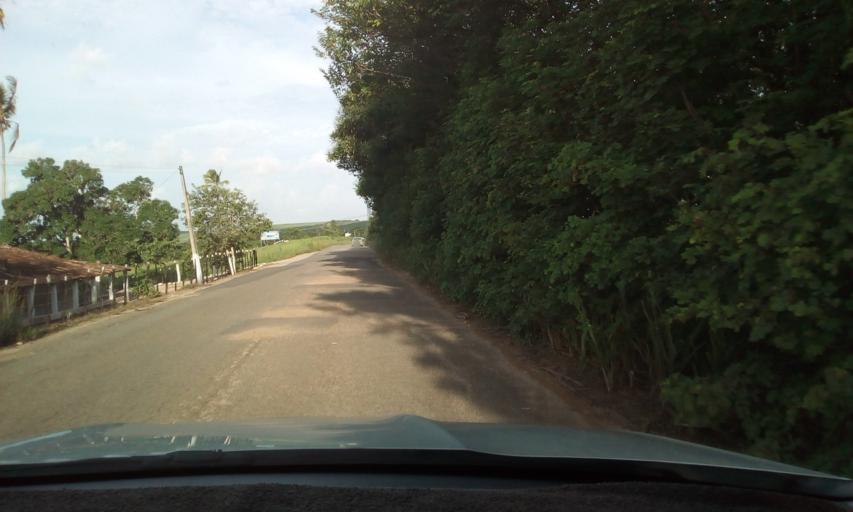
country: BR
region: Pernambuco
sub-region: Gloria Do Goita
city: Gloria do Goita
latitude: -7.9883
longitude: -35.2407
